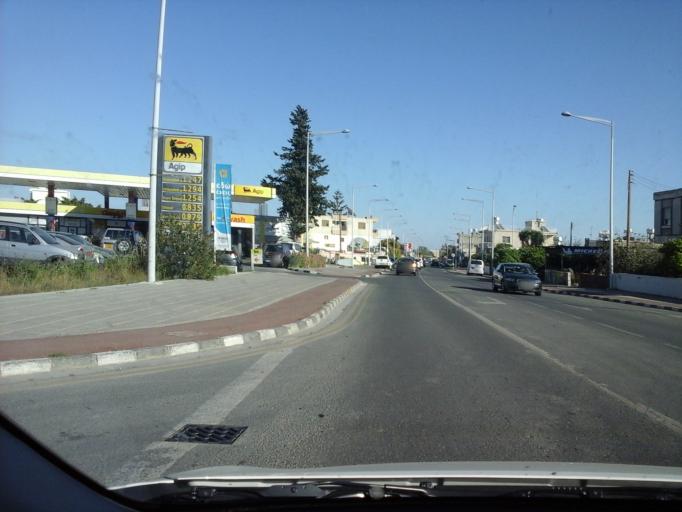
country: CY
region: Pafos
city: Paphos
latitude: 34.7634
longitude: 32.4490
